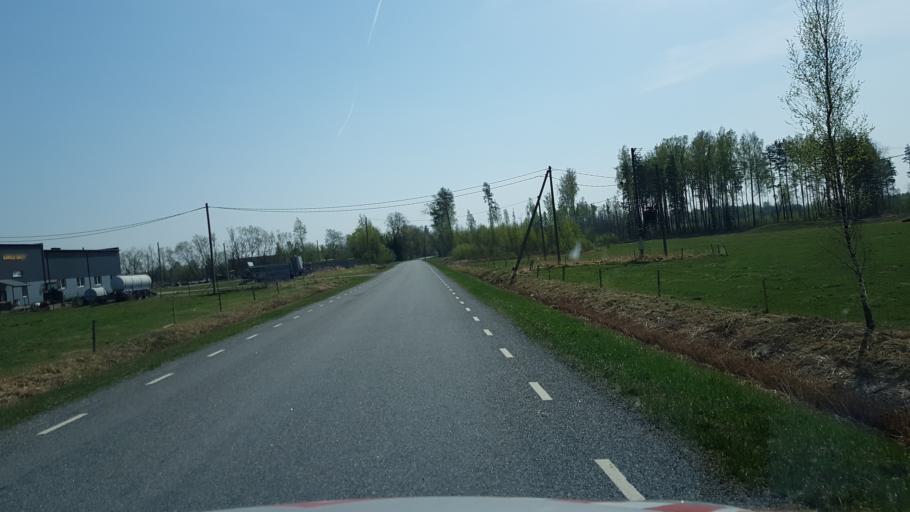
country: EE
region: Paernumaa
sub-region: Sindi linn
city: Sindi
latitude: 58.4302
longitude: 24.6415
